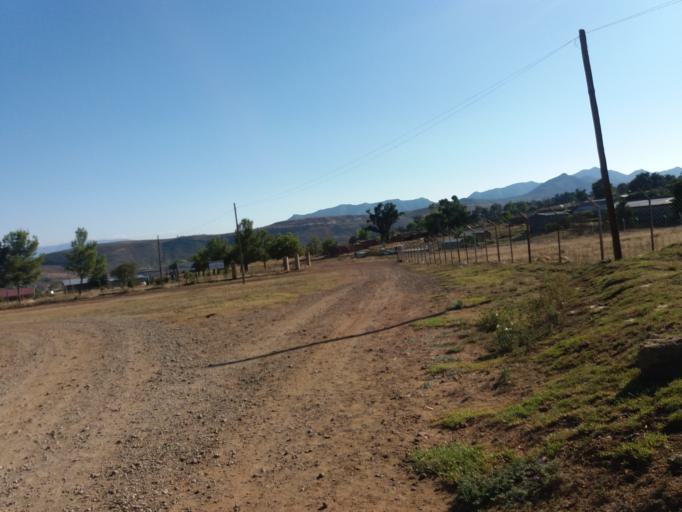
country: LS
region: Quthing
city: Quthing
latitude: -30.4098
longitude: 27.6964
